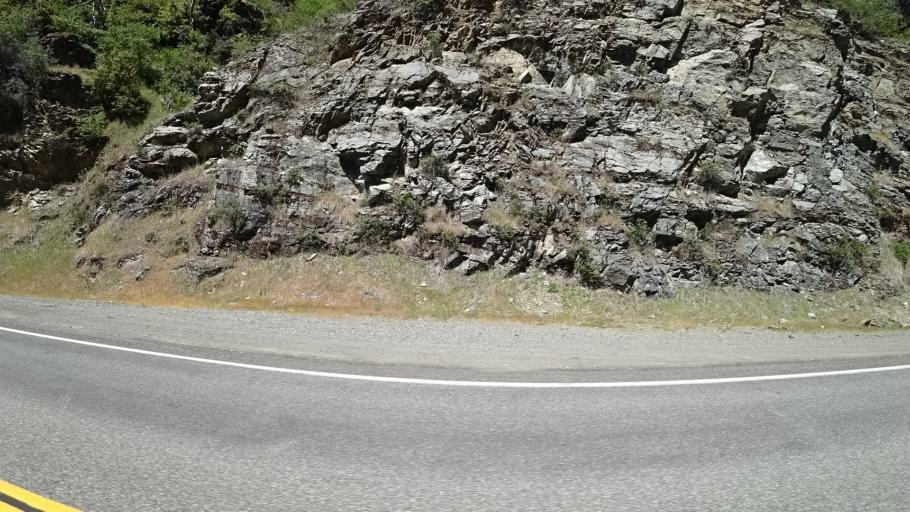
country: US
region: California
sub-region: Trinity County
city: Hayfork
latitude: 40.7519
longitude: -123.1616
